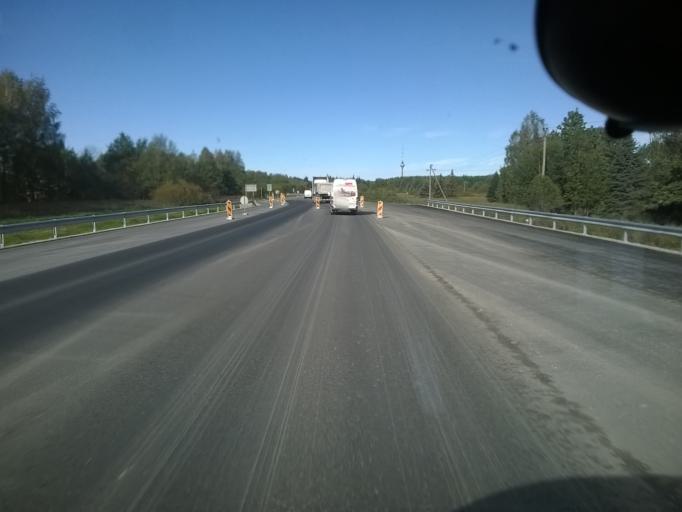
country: EE
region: Harju
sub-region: Joelaehtme vald
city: Loo
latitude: 59.4387
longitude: 24.9126
